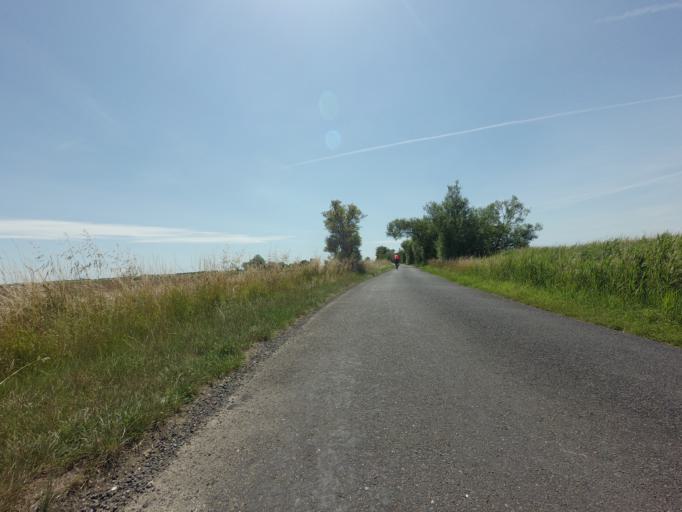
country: GB
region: England
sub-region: Kent
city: Lydd
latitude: 50.9842
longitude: 0.8950
